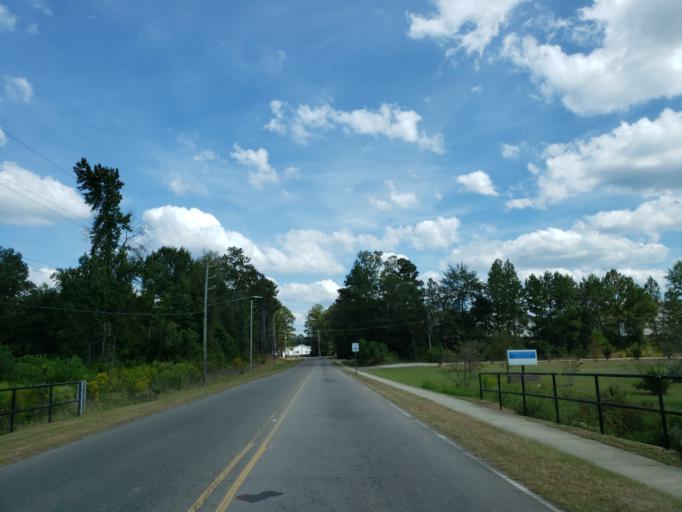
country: US
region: Mississippi
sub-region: Forrest County
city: Hattiesburg
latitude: 31.2992
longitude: -89.2988
